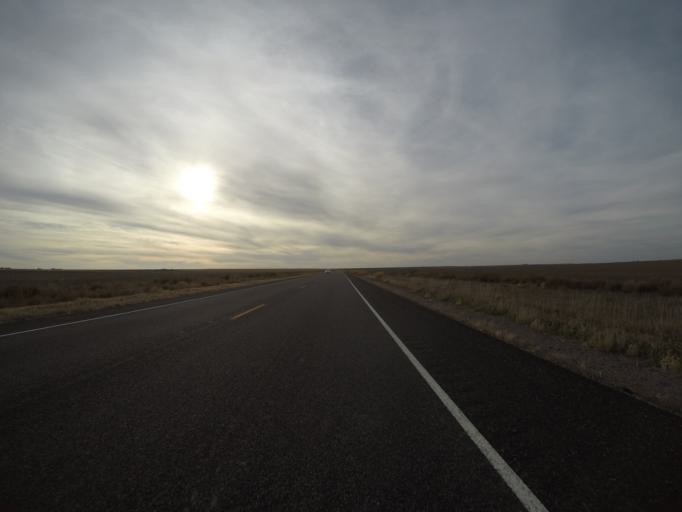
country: US
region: Kansas
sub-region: Cheyenne County
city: Saint Francis
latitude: 39.7462
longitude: -102.1131
